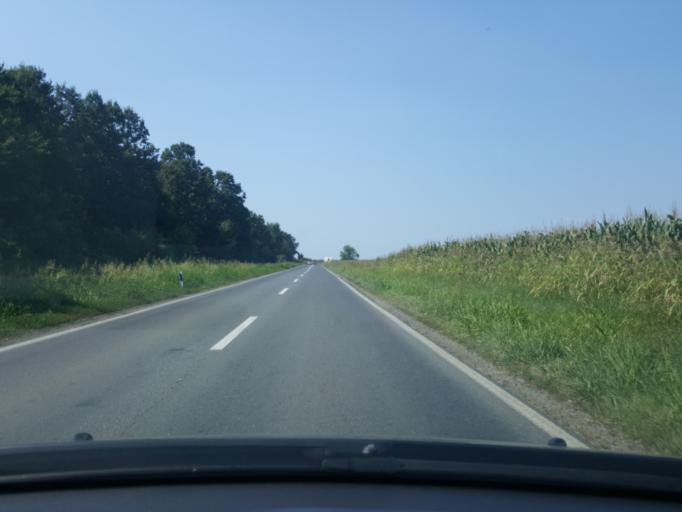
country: RS
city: Platicevo
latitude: 44.8401
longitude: 19.7695
